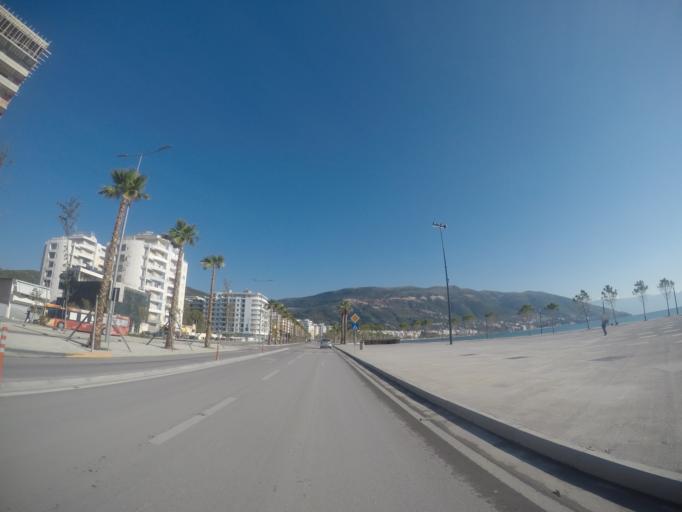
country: AL
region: Vlore
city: Vlore
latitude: 40.4510
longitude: 19.4889
